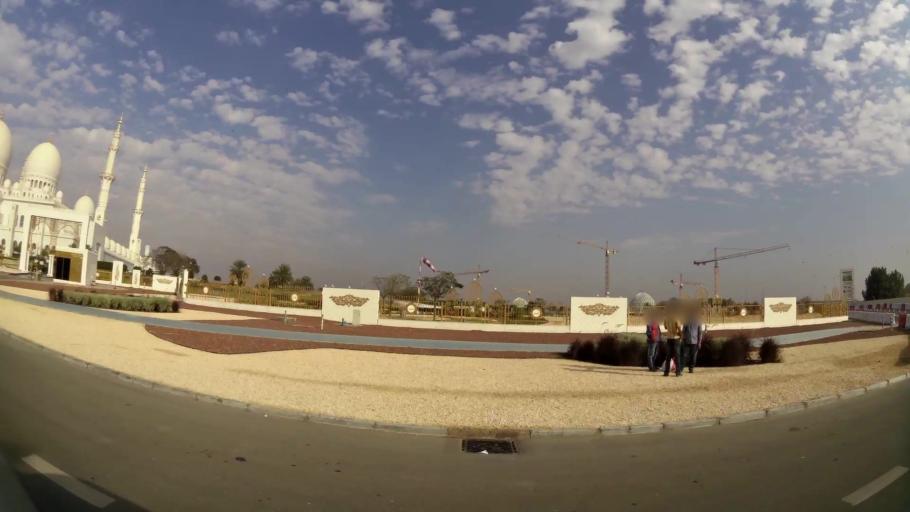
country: AE
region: Abu Dhabi
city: Abu Dhabi
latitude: 24.4097
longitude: 54.4718
